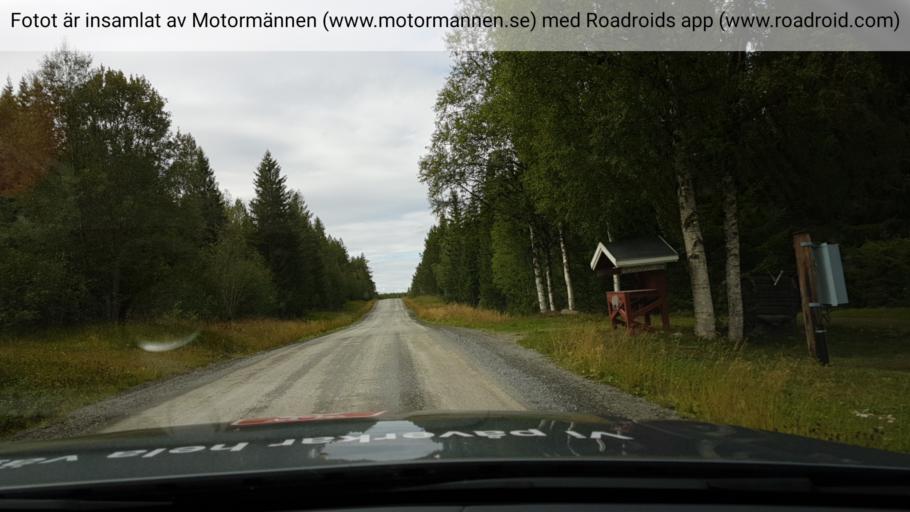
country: SE
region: Jaemtland
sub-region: Krokoms Kommun
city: Valla
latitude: 63.6670
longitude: 13.7121
